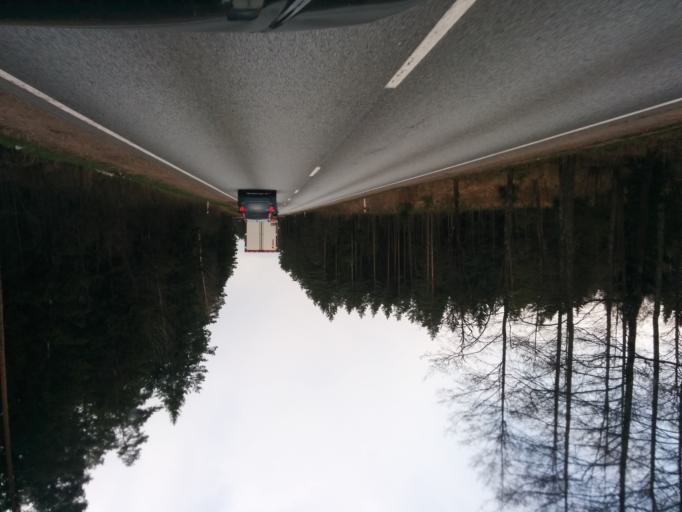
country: LV
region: Kekava
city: Balozi
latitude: 56.8260
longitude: 24.0630
